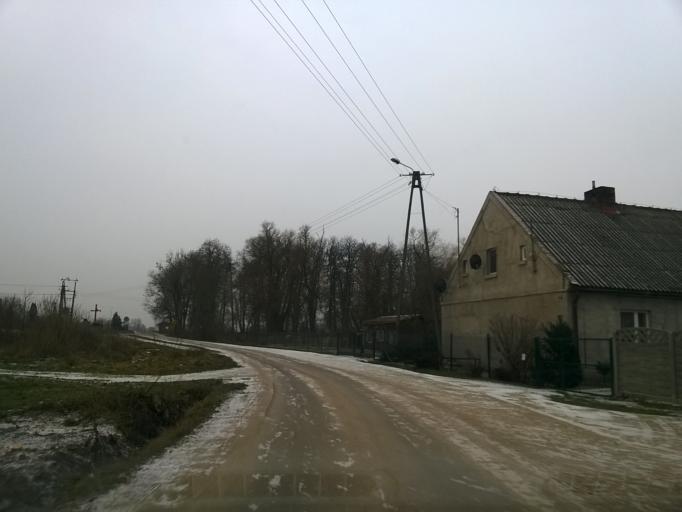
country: PL
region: Kujawsko-Pomorskie
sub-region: Powiat nakielski
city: Kcynia
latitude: 53.0096
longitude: 17.5009
